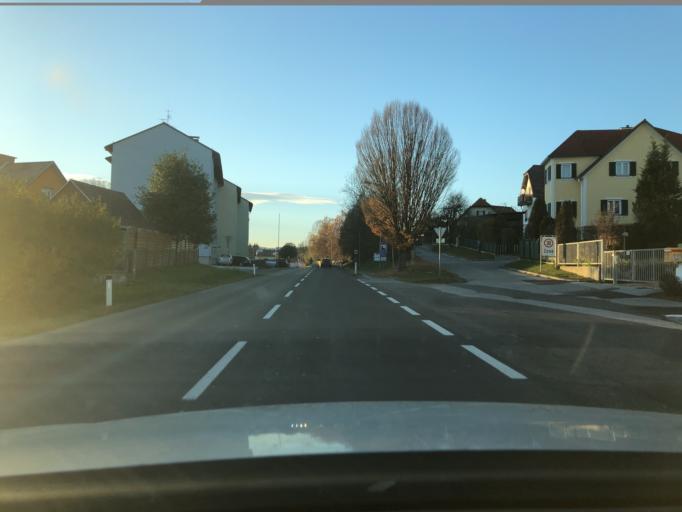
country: AT
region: Styria
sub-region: Politischer Bezirk Weiz
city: Gleisdorf
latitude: 47.1020
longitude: 15.7224
